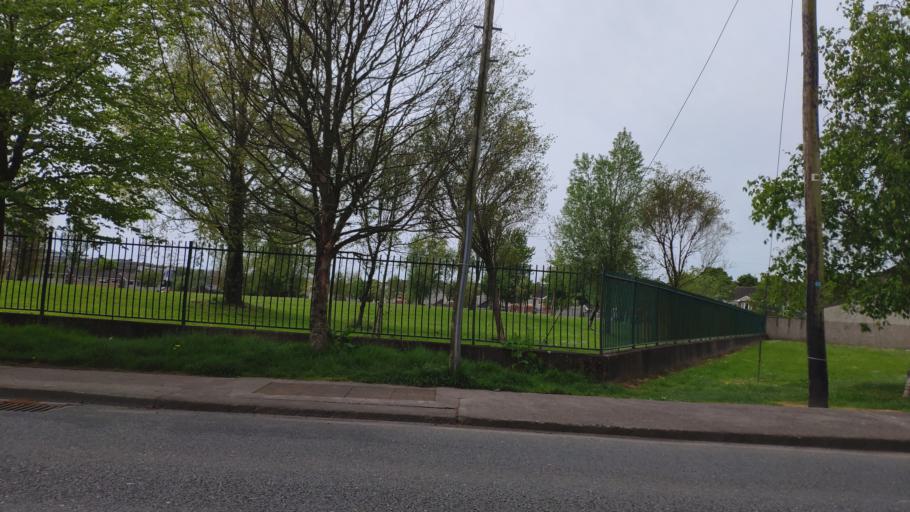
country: IE
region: Munster
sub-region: County Cork
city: Cork
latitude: 51.9204
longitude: -8.4544
